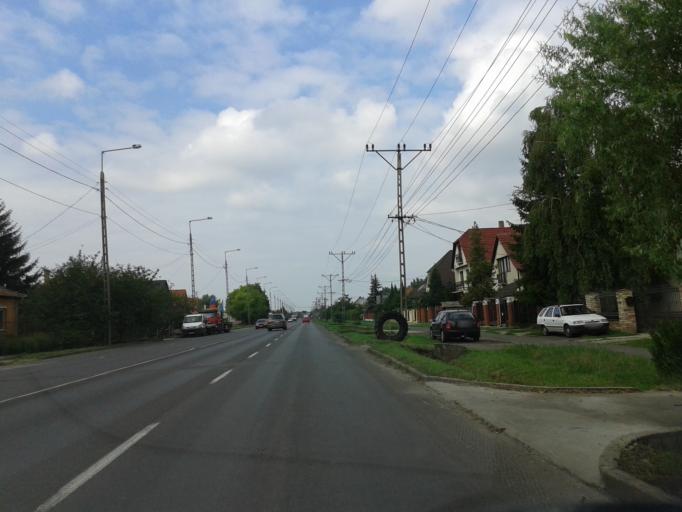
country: HU
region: Csongrad
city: Szeged
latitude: 46.2709
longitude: 20.0883
